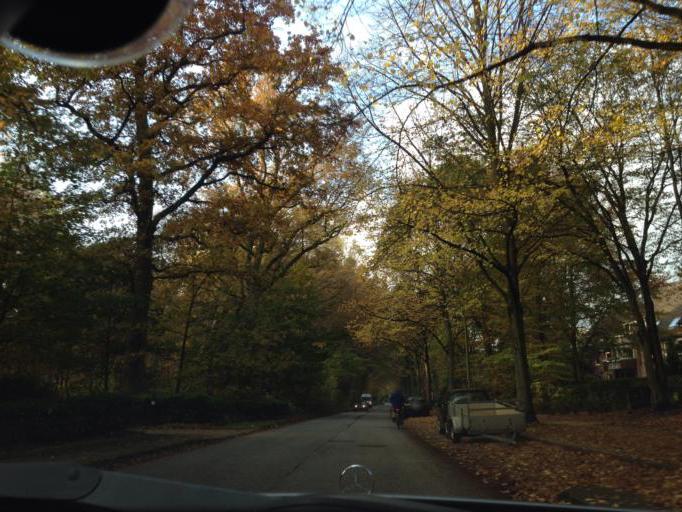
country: DE
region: Schleswig-Holstein
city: Barsbuettel
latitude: 53.5920
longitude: 10.1738
